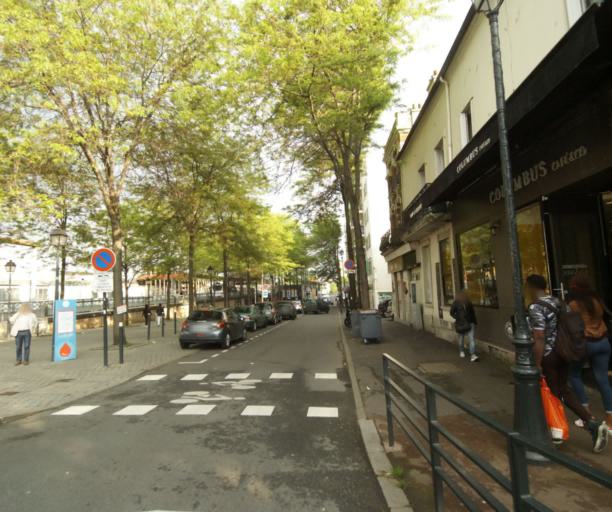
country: FR
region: Ile-de-France
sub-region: Departement du Val-d'Oise
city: Argenteuil
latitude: 48.9418
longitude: 2.2594
